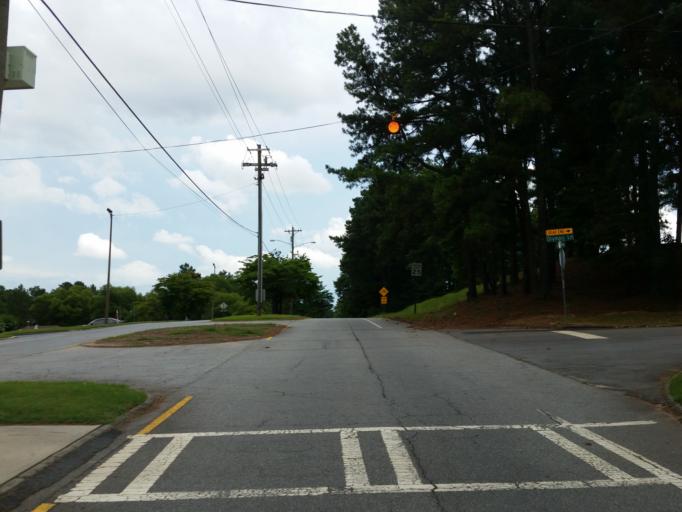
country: US
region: Georgia
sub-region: Cobb County
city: Kennesaw
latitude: 34.0373
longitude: -84.5939
